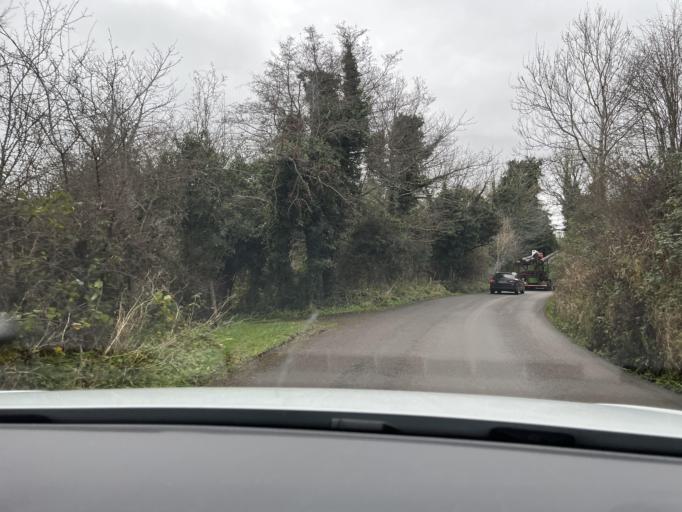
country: IE
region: Connaught
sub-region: County Leitrim
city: Manorhamilton
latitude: 54.2307
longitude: -8.2842
